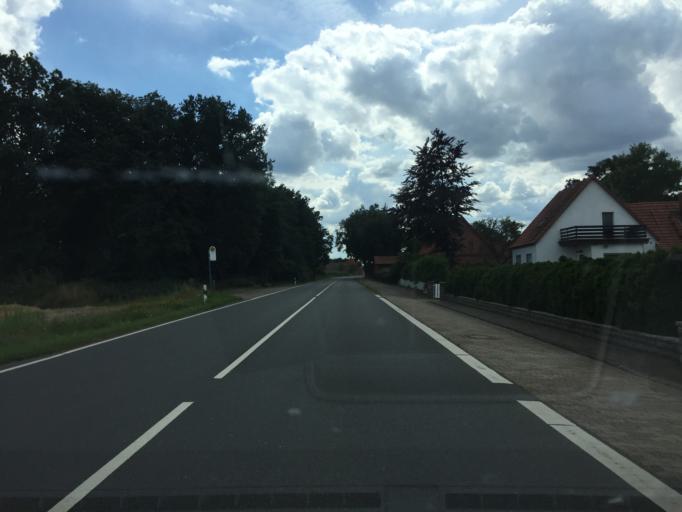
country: DE
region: Lower Saxony
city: Heemsen
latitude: 52.7210
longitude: 9.2857
